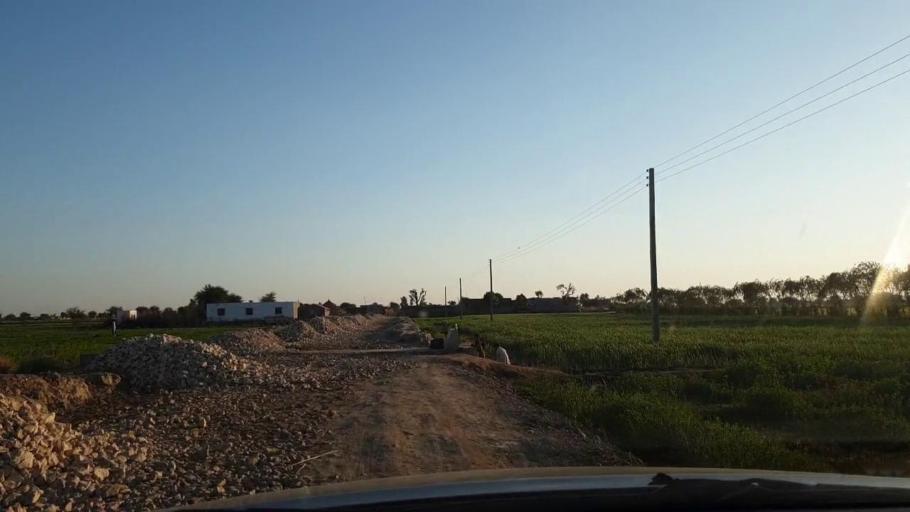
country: PK
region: Sindh
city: Tando Mittha Khan
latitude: 25.8350
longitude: 69.1614
